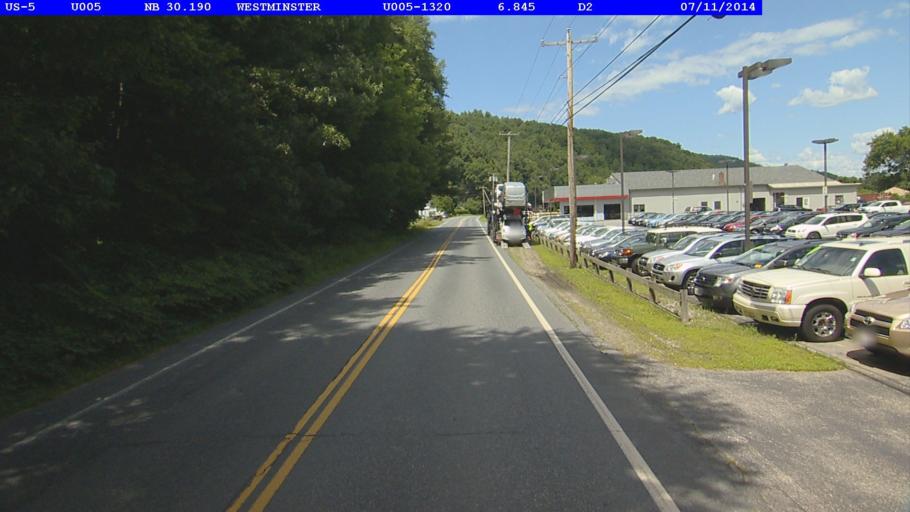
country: US
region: Vermont
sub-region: Windham County
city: Bellows Falls
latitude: 43.1079
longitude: -72.4420
